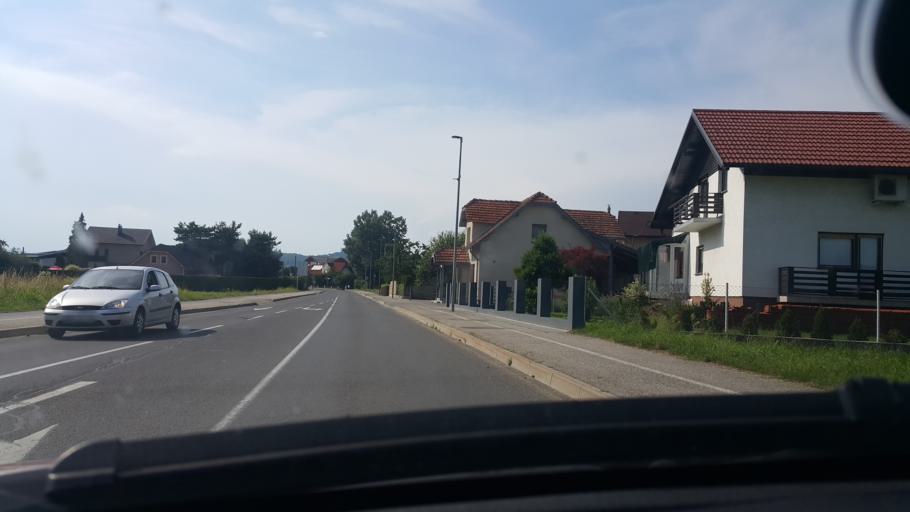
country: SI
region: Duplek
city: Spodnji Duplek
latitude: 46.5015
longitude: 15.7508
